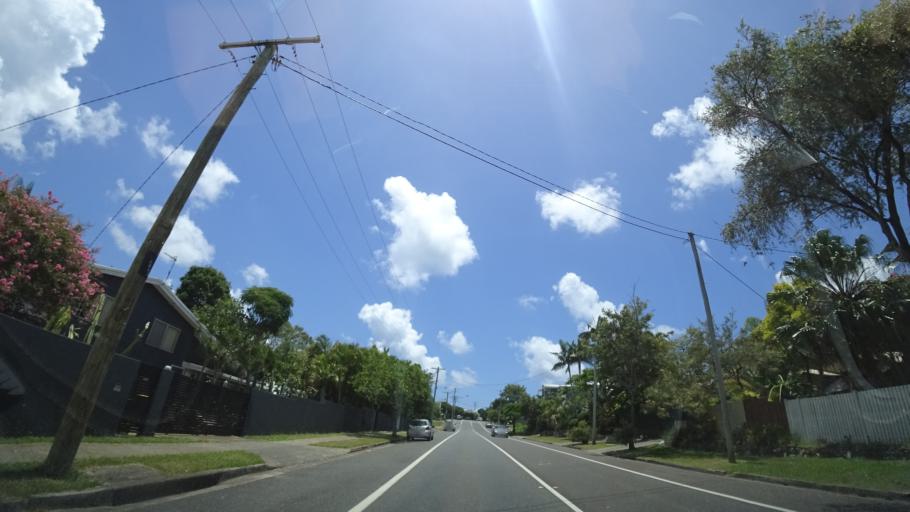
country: AU
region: Queensland
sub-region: Sunshine Coast
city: Coolum Beach
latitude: -26.5341
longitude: 153.0869
